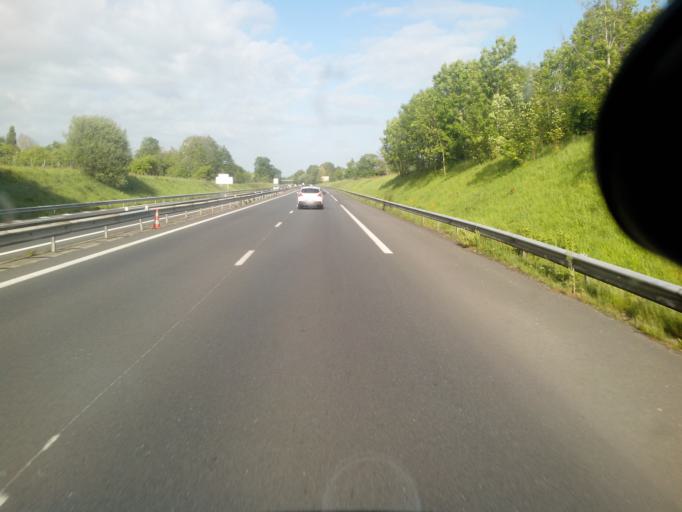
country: FR
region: Lower Normandy
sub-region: Departement du Calvados
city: Touques
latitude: 49.2577
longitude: 0.0962
